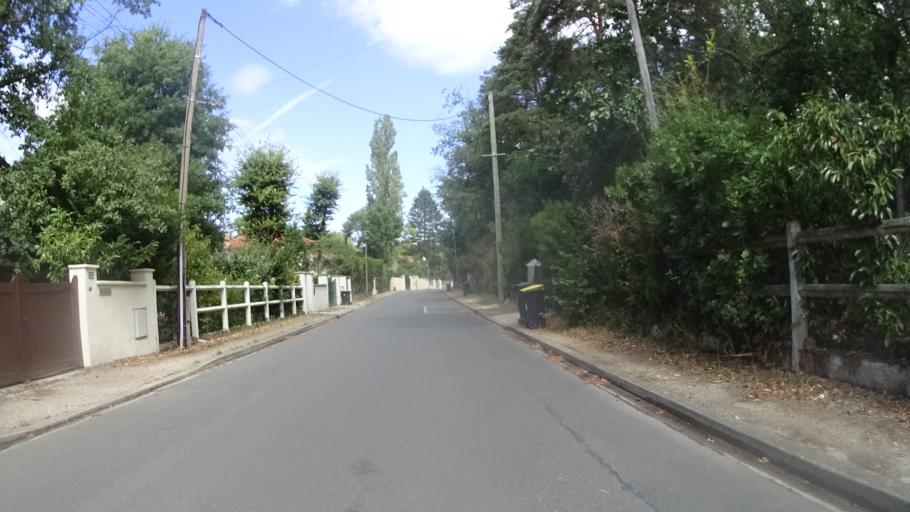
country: FR
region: Centre
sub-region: Departement du Loiret
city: Malesherbes
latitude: 48.2908
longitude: 2.4310
